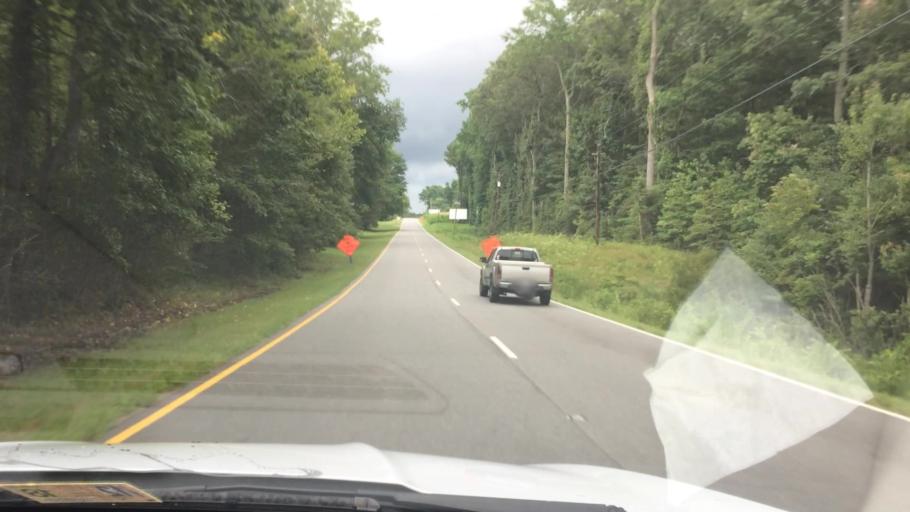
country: US
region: Virginia
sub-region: King William County
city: West Point
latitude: 37.4031
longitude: -76.8242
